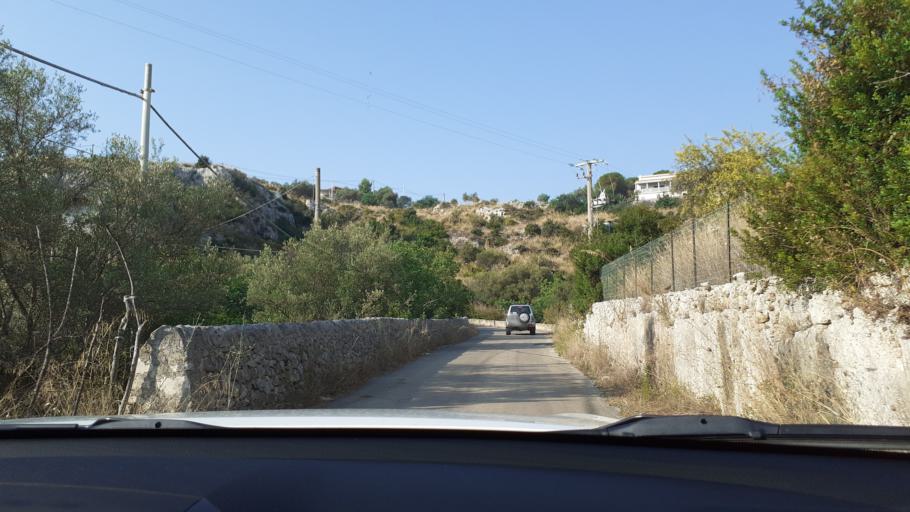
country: IT
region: Sicily
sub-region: Provincia di Siracusa
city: Cassibile
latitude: 36.9789
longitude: 15.1598
